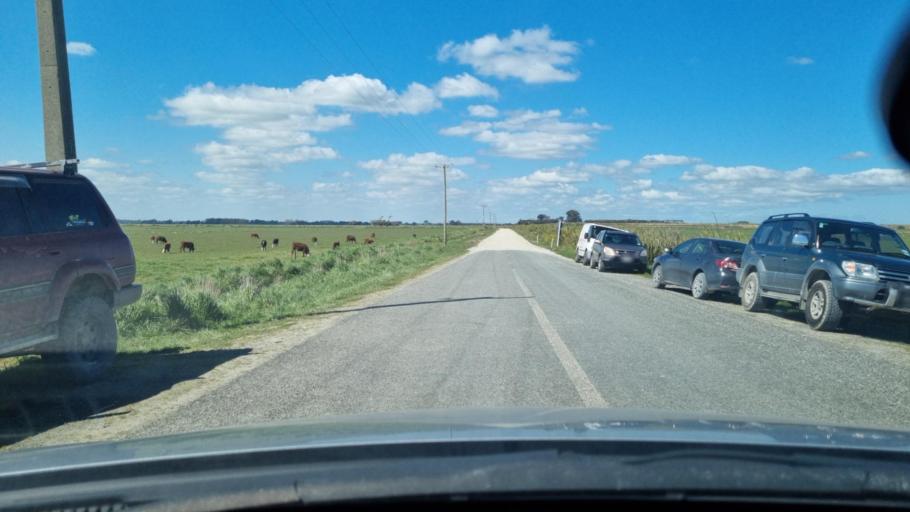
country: NZ
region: Southland
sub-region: Invercargill City
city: Invercargill
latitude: -46.3934
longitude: 168.2396
